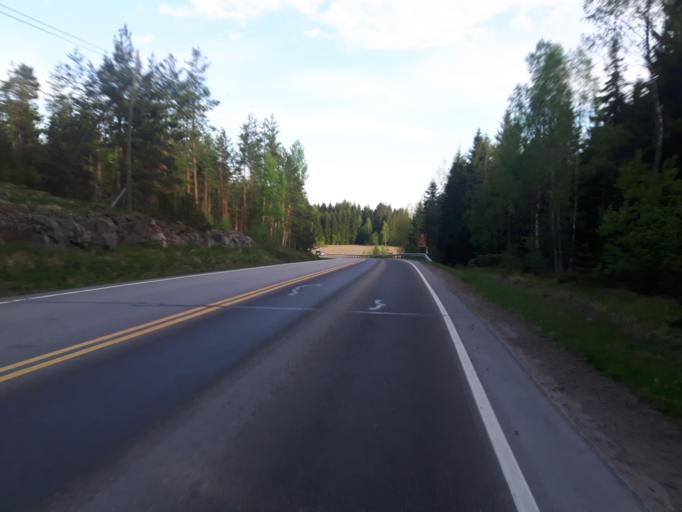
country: FI
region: Uusimaa
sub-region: Loviisa
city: Perna
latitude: 60.4672
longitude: 26.0307
